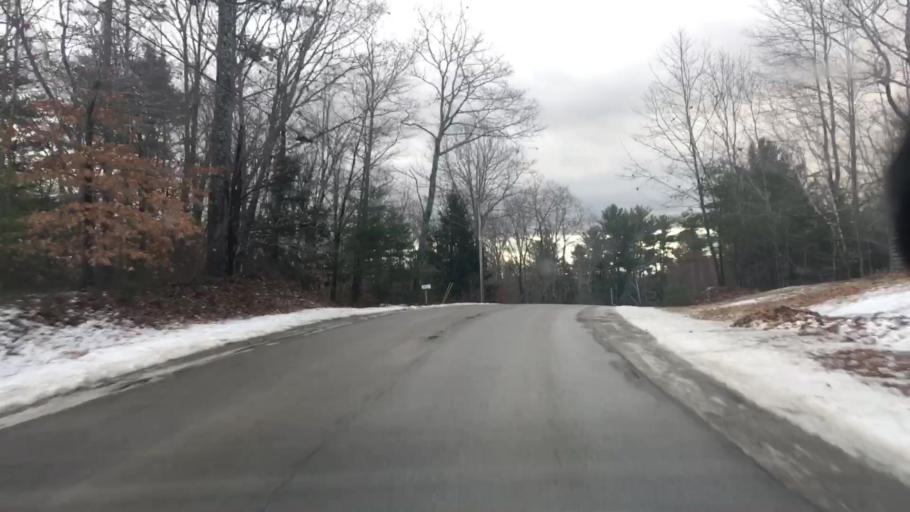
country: US
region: Maine
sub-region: Hancock County
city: Dedham
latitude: 44.6383
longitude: -68.7045
